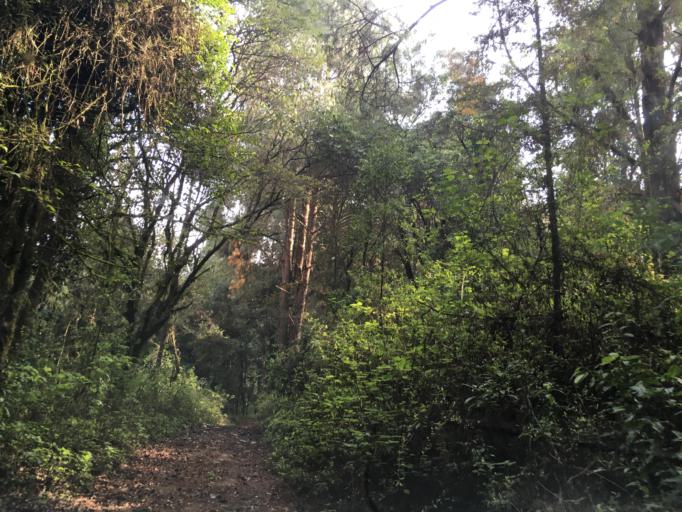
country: MX
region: Michoacan
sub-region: Zitacuaro
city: Francisco Serrato (San Bartolo)
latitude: 19.5170
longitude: -100.3026
